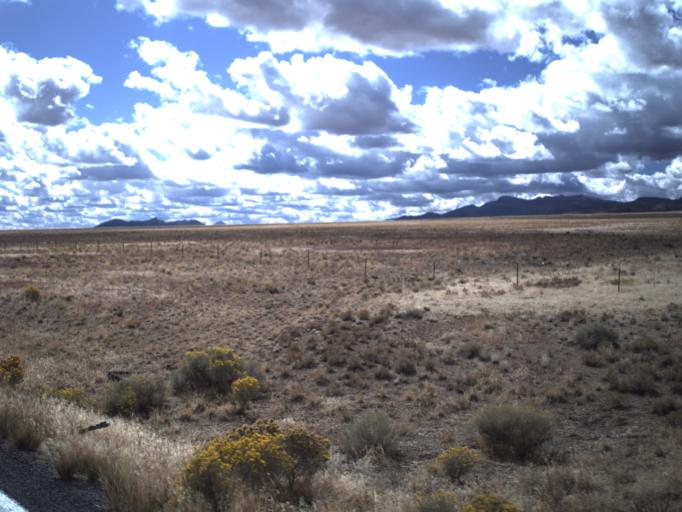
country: US
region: Utah
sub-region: Beaver County
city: Milford
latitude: 38.6765
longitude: -113.8892
